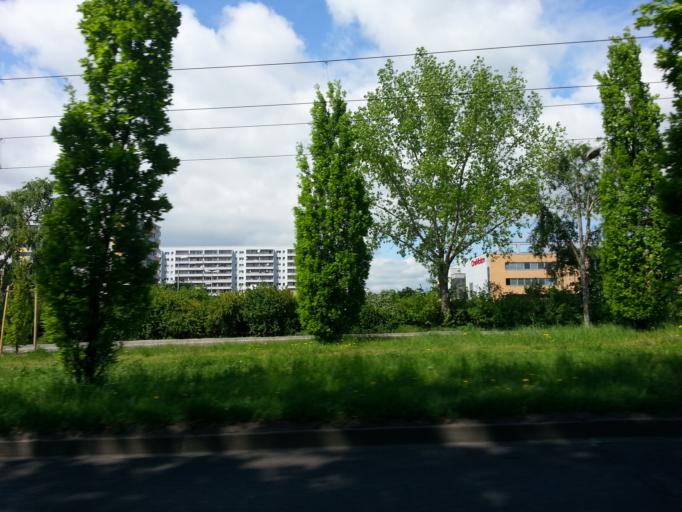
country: DE
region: Berlin
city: Neu-Hohenschoenhausen
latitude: 52.5647
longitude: 13.5094
